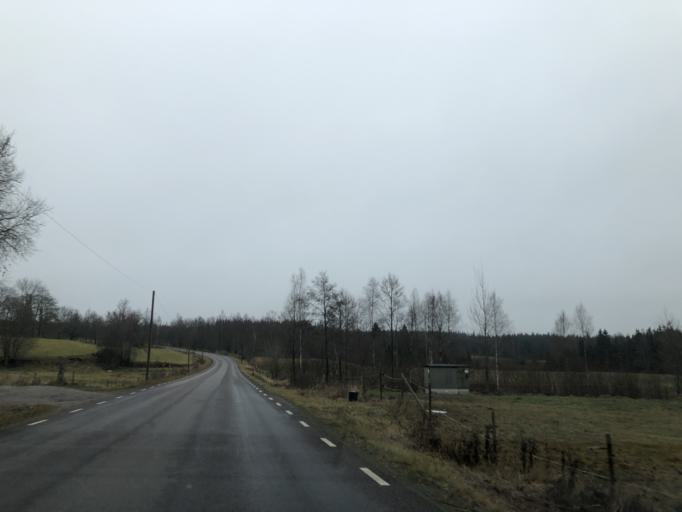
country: SE
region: Vaestra Goetaland
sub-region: Ulricehamns Kommun
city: Ulricehamn
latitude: 57.7241
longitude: 13.5501
